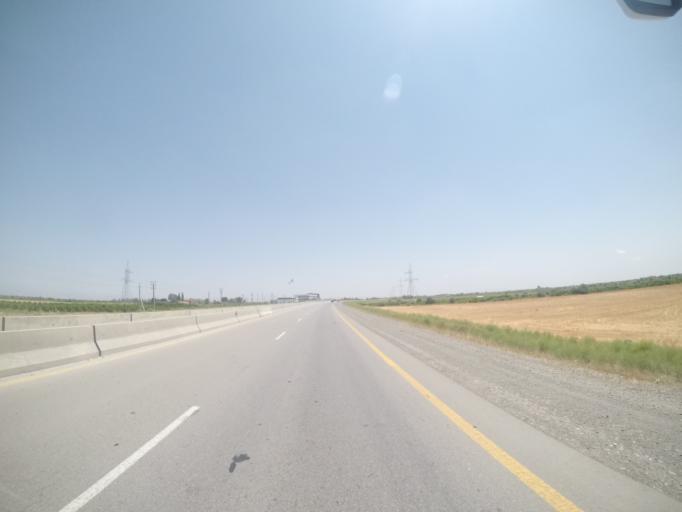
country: AZ
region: Kurdamir Rayon
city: Kyurdarmir
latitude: 40.3207
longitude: 48.1852
